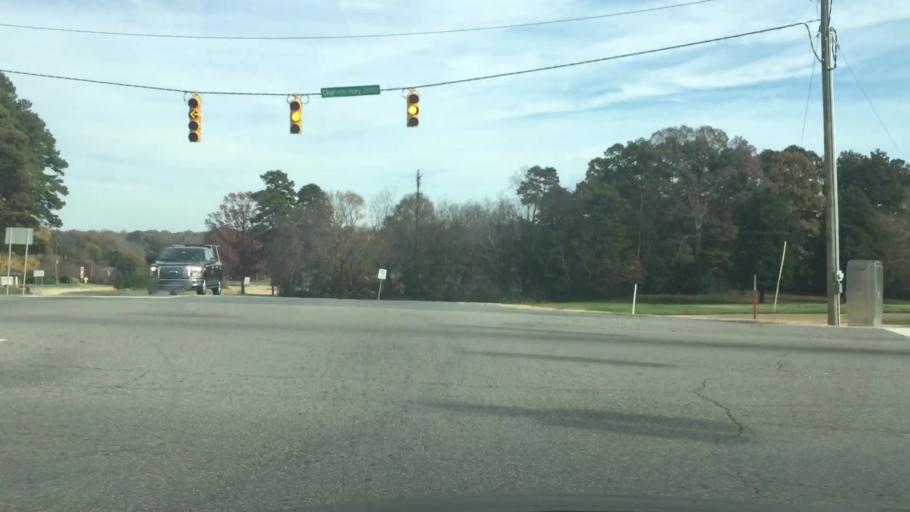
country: US
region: North Carolina
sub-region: Iredell County
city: Mooresville
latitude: 35.5791
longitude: -80.8403
